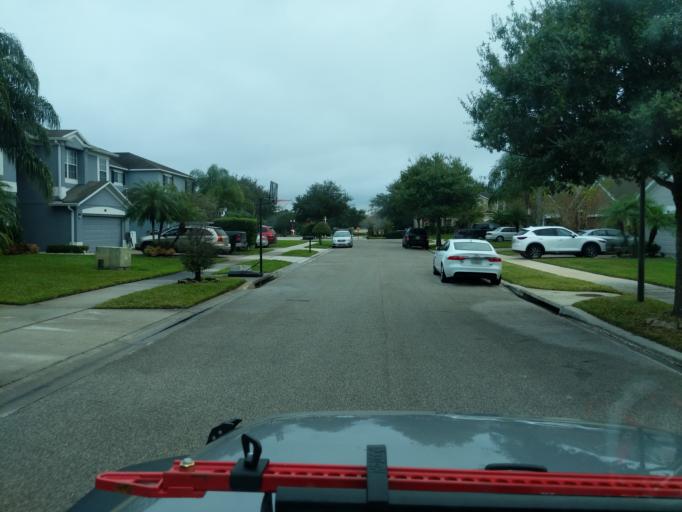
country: US
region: Florida
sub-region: Orange County
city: Winter Garden
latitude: 28.5332
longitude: -81.5833
